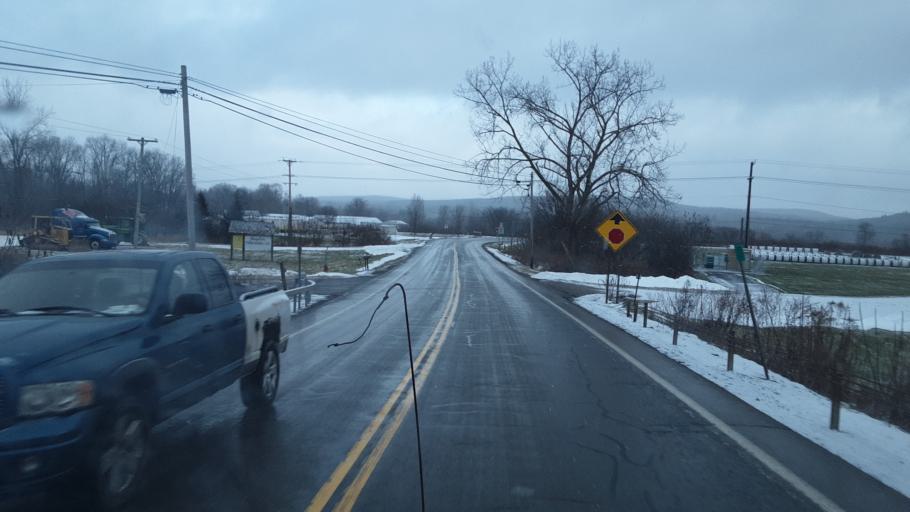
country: US
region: New York
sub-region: Allegany County
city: Houghton
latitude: 42.3278
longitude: -78.1130
